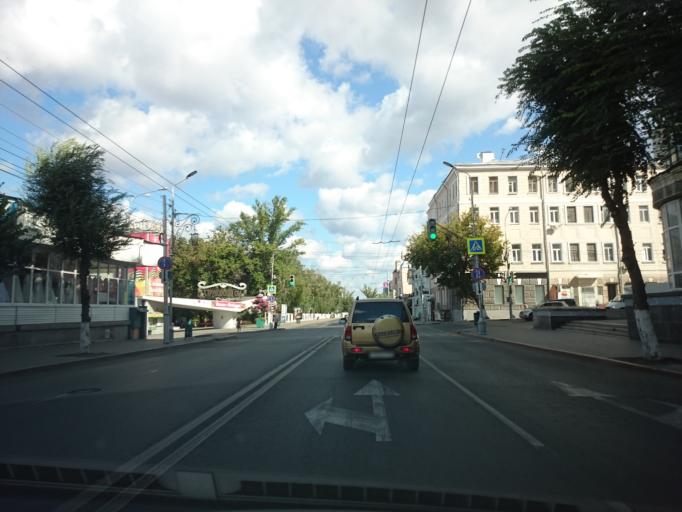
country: RU
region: Samara
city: Rozhdestveno
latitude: 53.1946
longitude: 50.0936
